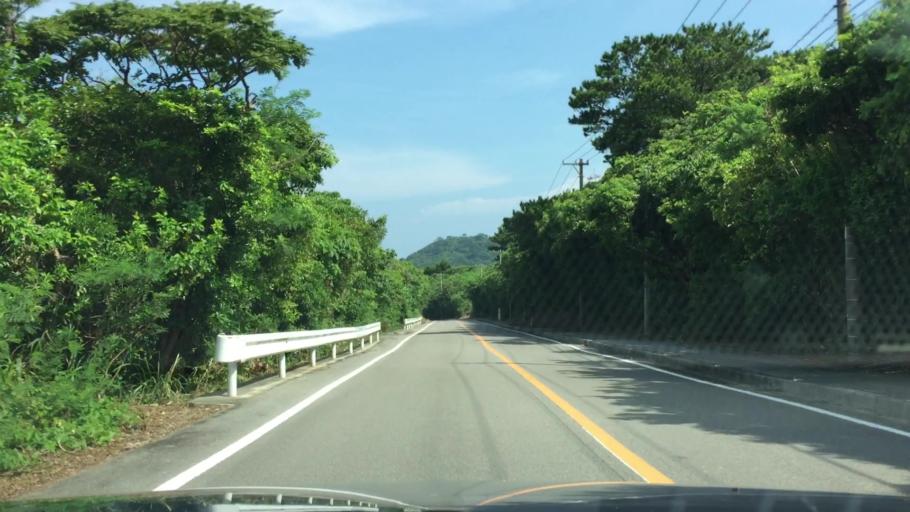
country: JP
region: Okinawa
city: Ishigaki
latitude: 24.5115
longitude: 124.2672
